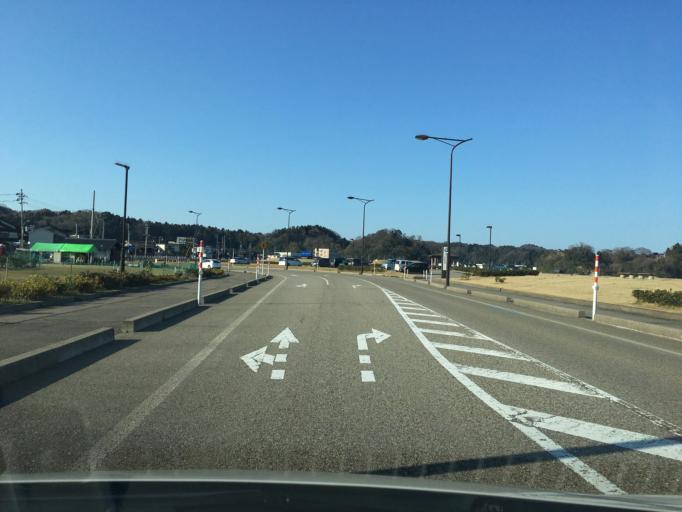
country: JP
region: Toyama
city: Himi
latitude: 36.8732
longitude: 136.9846
